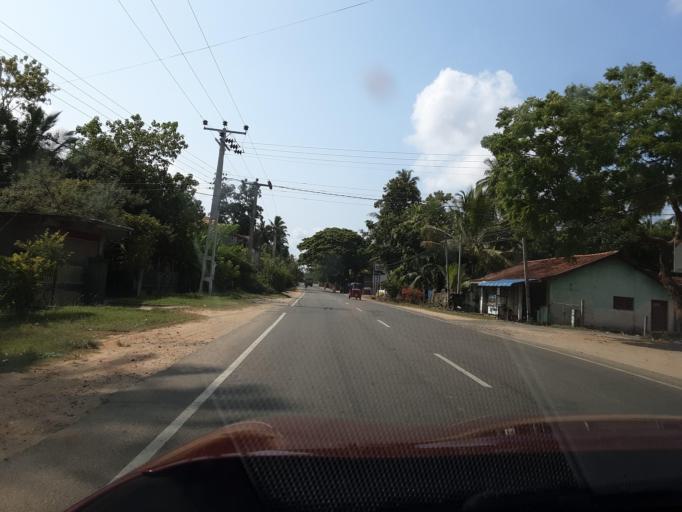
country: LK
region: Southern
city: Tangalla
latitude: 6.3045
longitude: 81.2344
